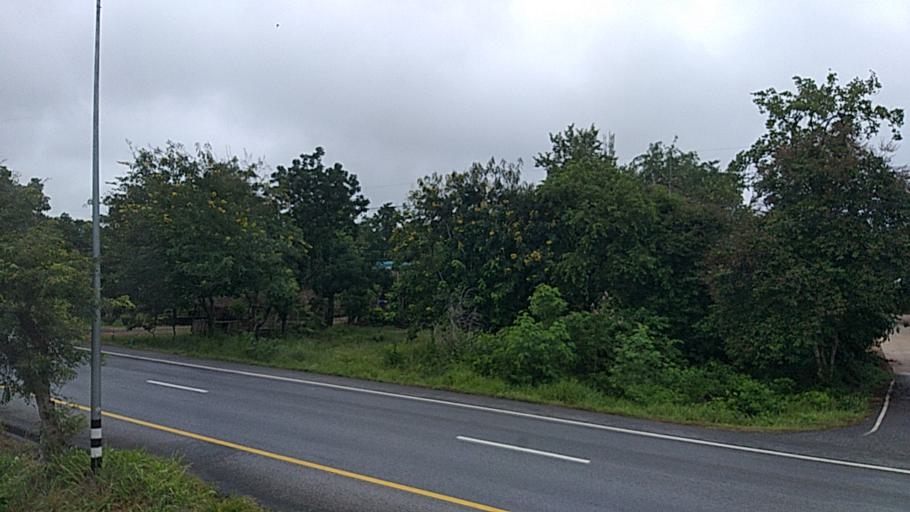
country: TH
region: Nakhon Ratchasima
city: Non Daeng
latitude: 15.3559
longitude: 102.4498
